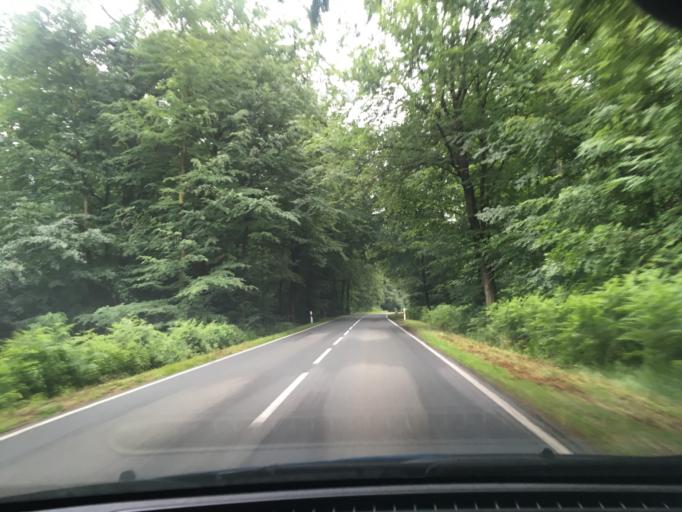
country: DE
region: Lower Saxony
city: Garlstorf
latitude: 53.2202
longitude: 10.0818
